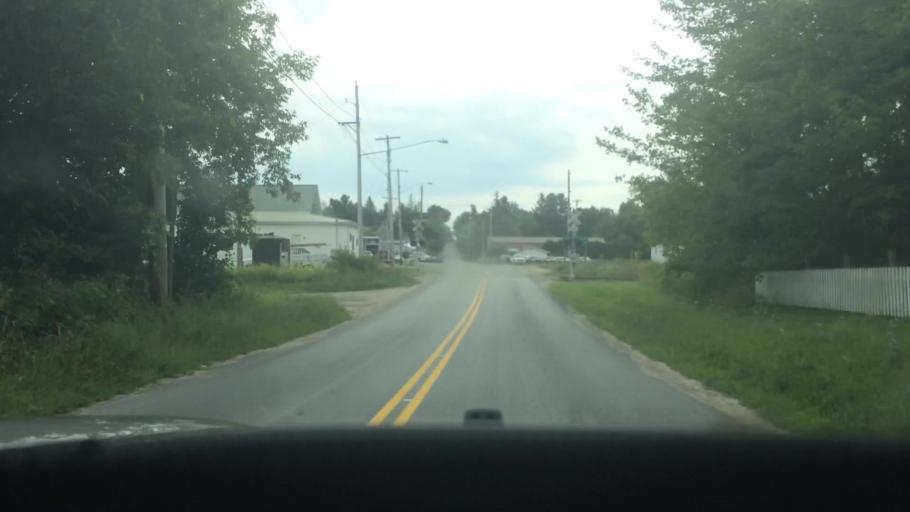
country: US
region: New York
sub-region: St. Lawrence County
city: Canton
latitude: 44.5062
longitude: -75.2749
